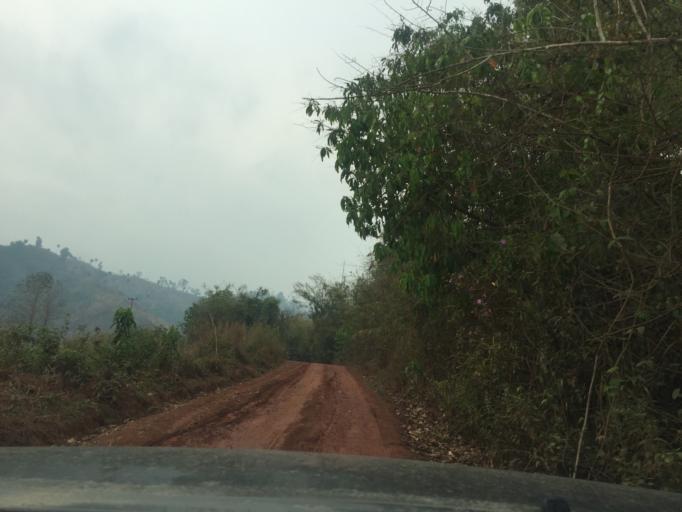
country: TH
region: Nan
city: Bo Kluea
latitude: 18.8424
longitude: 101.4095
